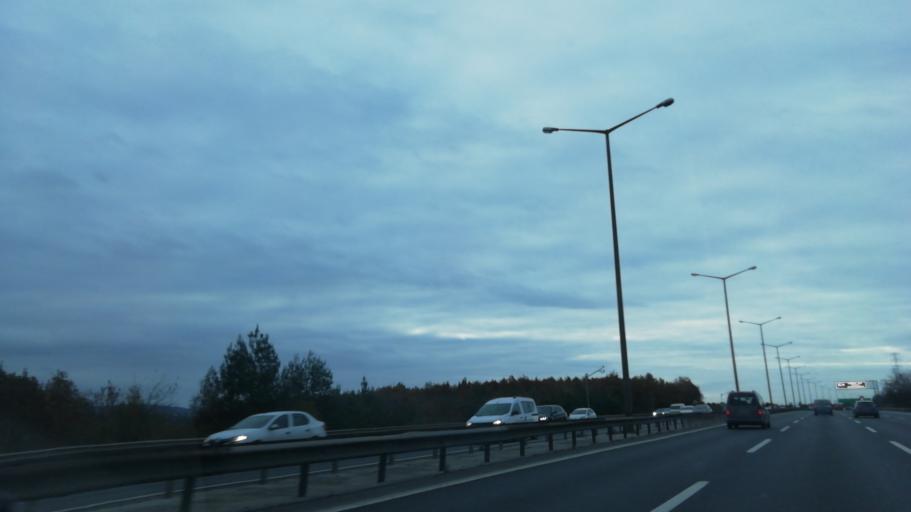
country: TR
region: Istanbul
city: Umraniye
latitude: 41.0651
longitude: 29.1116
